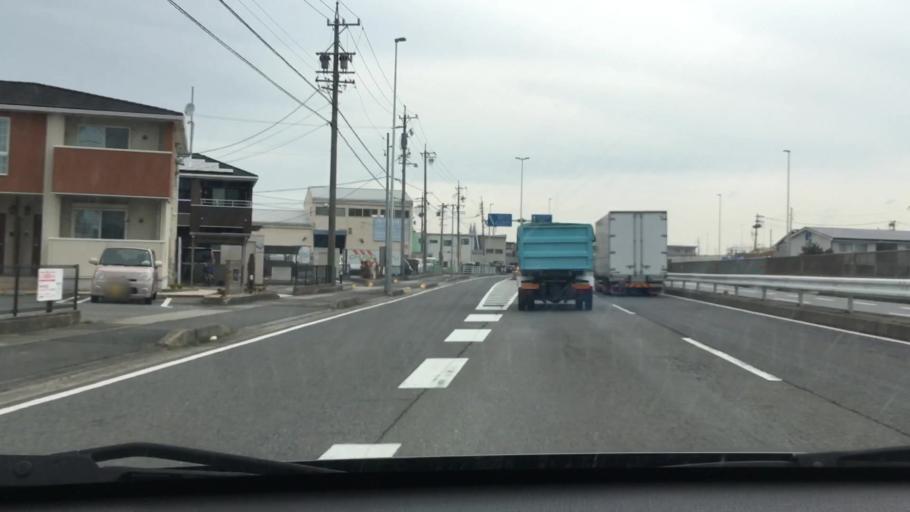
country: JP
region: Mie
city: Yokkaichi
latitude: 34.9307
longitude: 136.5950
